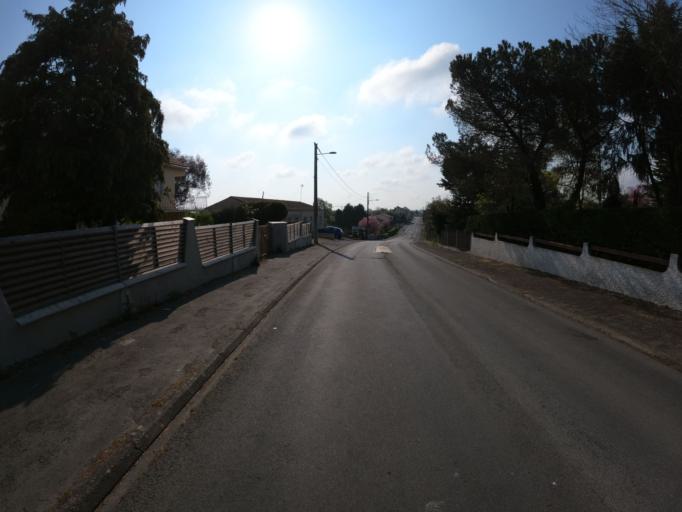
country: FR
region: Pays de la Loire
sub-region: Departement de Maine-et-Loire
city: La Romagne
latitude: 47.0630
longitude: -1.0268
